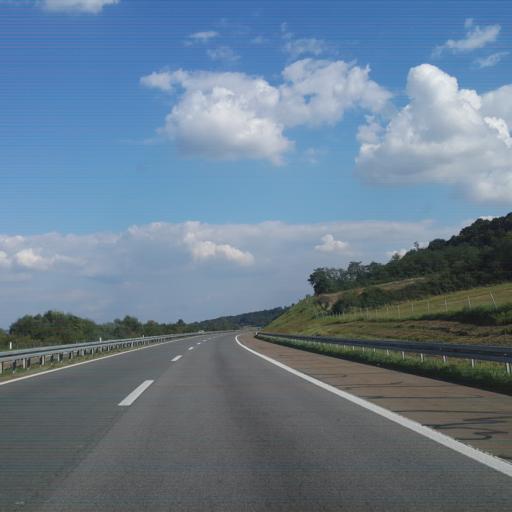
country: RS
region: Central Serbia
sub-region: Belgrade
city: Grocka
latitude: 44.5794
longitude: 20.7791
